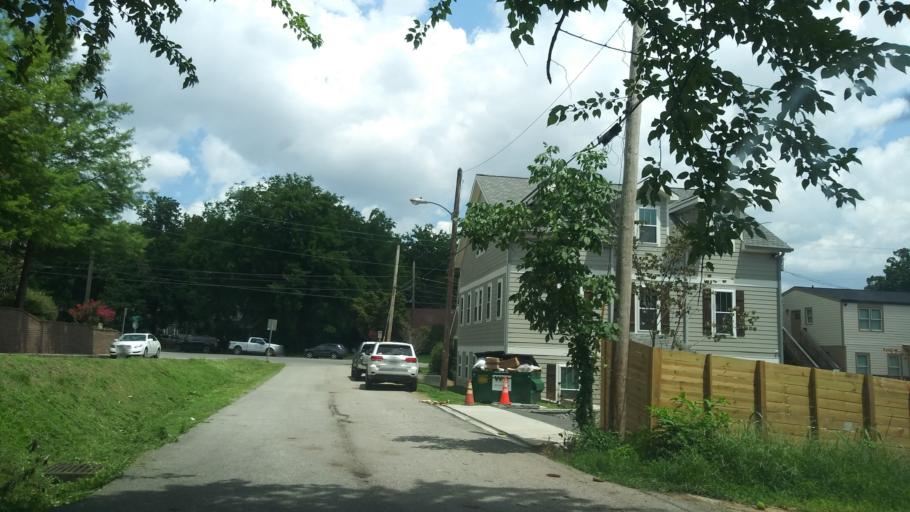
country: US
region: Tennessee
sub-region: Davidson County
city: Nashville
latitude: 36.1277
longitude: -86.7790
